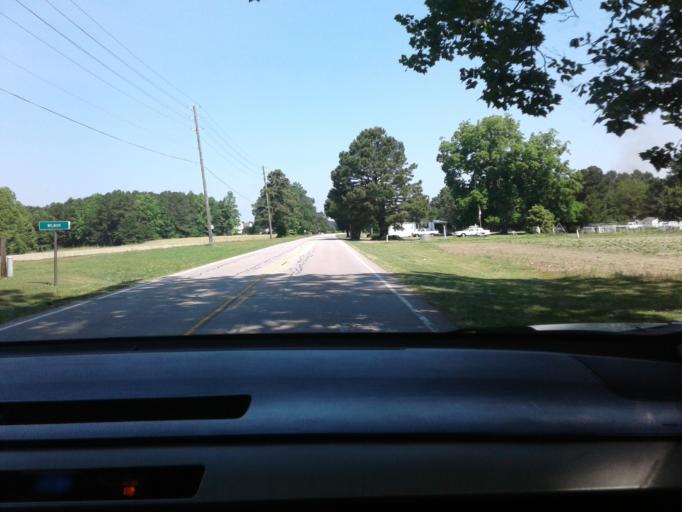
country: US
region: North Carolina
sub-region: Wake County
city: Fuquay-Varina
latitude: 35.6000
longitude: -78.8380
